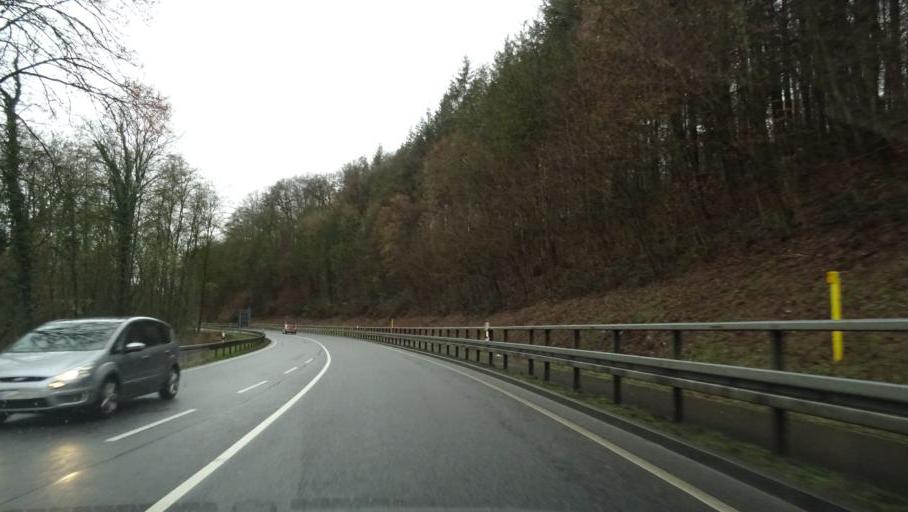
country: DE
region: Baden-Wuerttemberg
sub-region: Karlsruhe Region
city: Aglasterhausen
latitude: 49.3398
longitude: 8.9737
